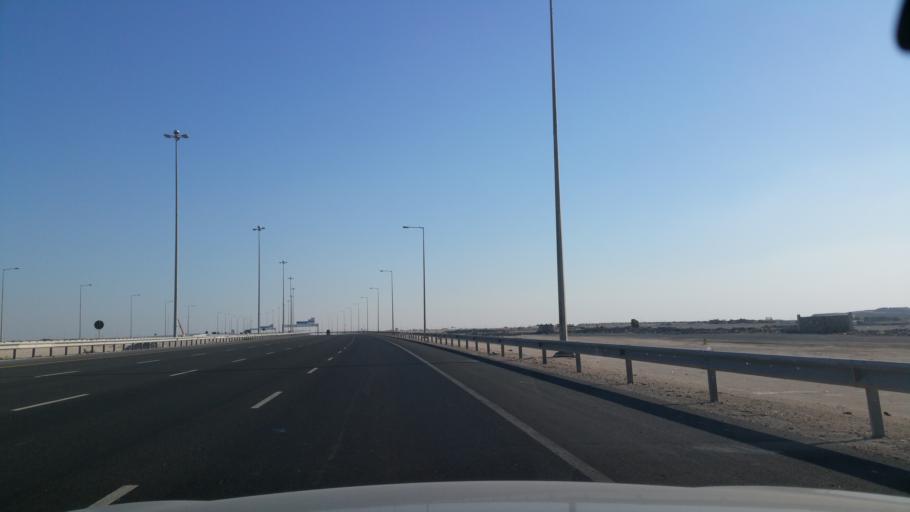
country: QA
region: Al Wakrah
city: Al Wukayr
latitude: 25.1468
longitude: 51.4746
